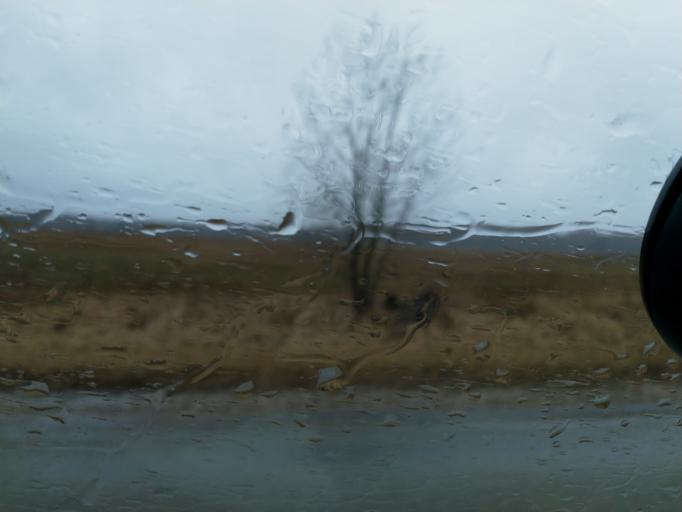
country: LV
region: Saldus Rajons
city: Saldus
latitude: 56.7856
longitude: 22.3274
